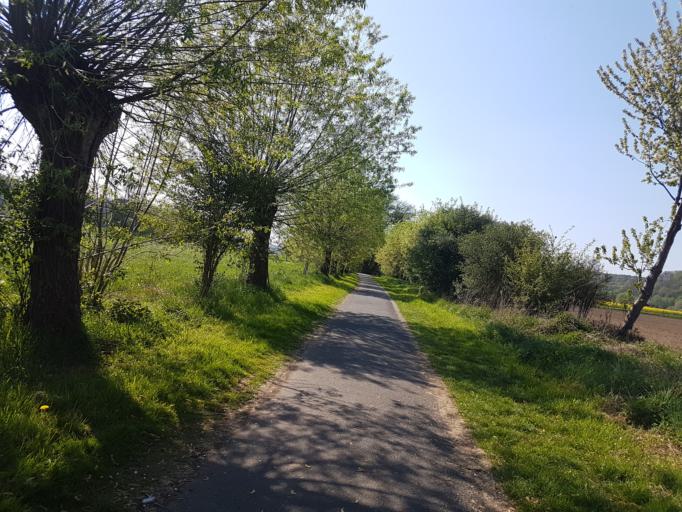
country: DE
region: North Rhine-Westphalia
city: Hattingen
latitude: 51.4168
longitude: 7.2243
